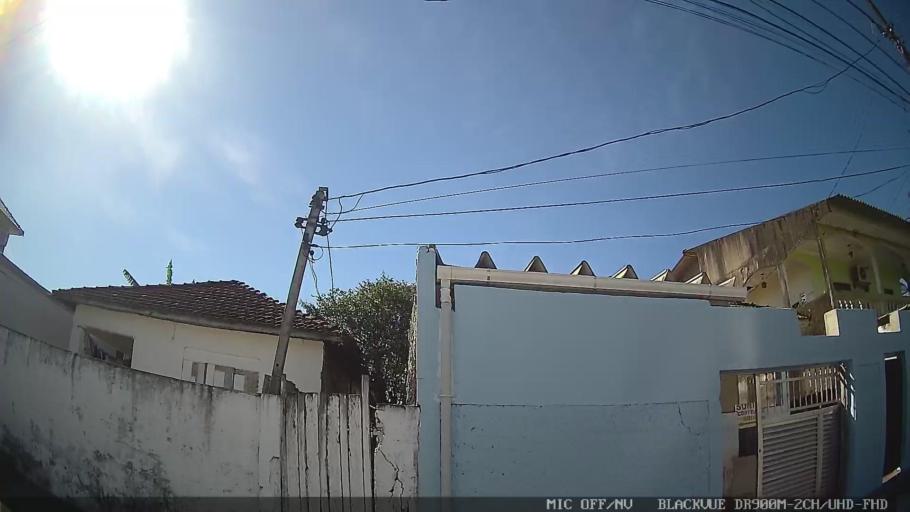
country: BR
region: Sao Paulo
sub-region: Santos
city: Santos
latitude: -23.9389
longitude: -46.2945
